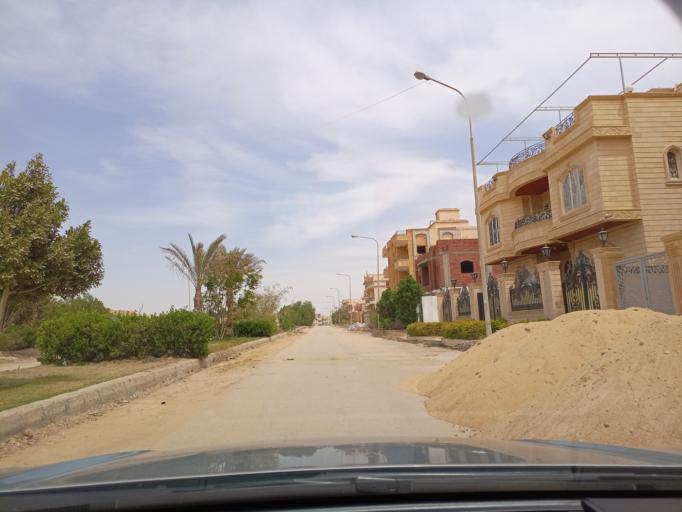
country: EG
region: Muhafazat al Qalyubiyah
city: Al Khankah
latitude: 30.2409
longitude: 31.4934
